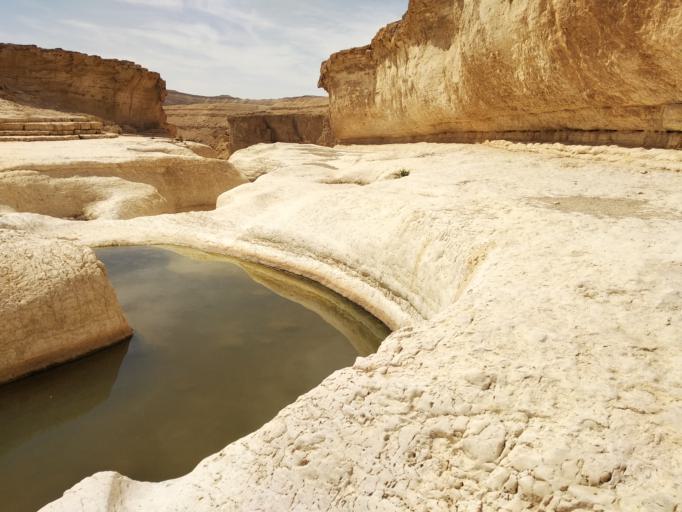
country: JO
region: Karak
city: Safi
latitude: 31.0094
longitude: 35.2886
